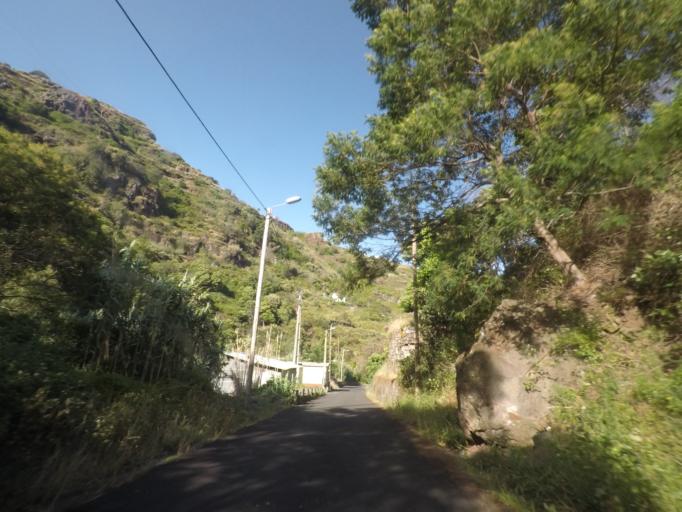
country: PT
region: Madeira
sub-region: Santa Cruz
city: Santa Cruz
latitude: 32.6931
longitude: -16.8034
